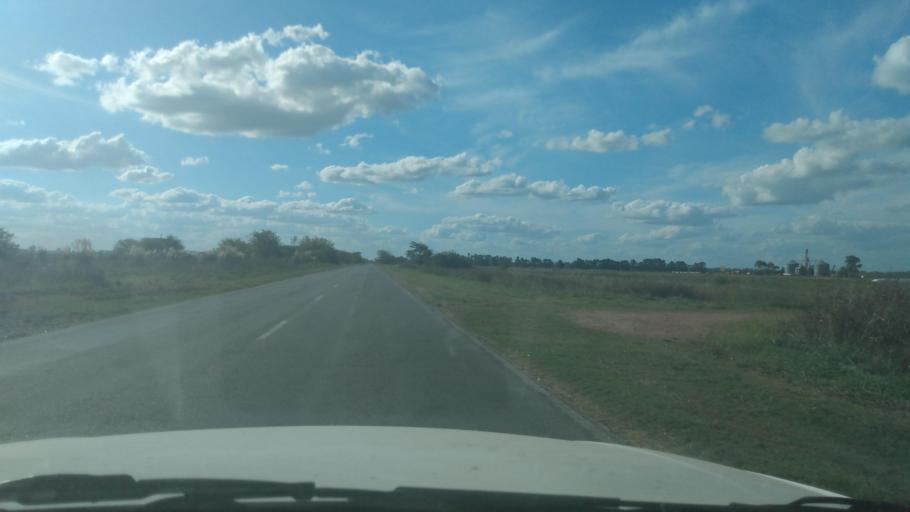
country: AR
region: Buenos Aires
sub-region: Partido de Navarro
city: Navarro
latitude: -34.9760
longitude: -59.3167
